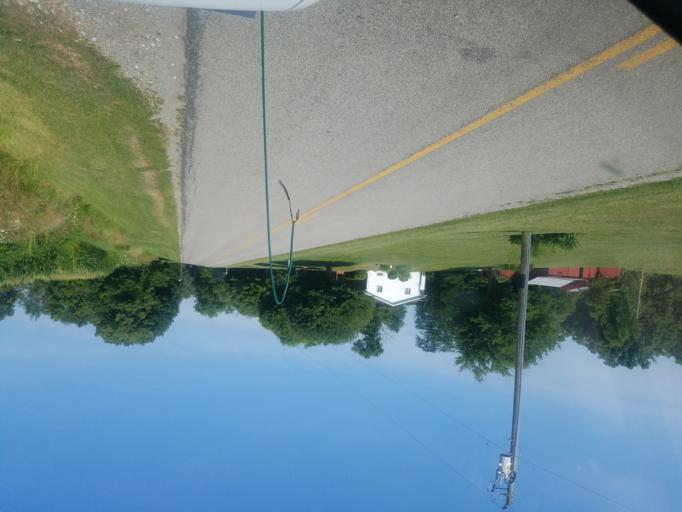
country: US
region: Ohio
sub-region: Union County
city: Marysville
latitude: 40.2819
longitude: -83.2576
